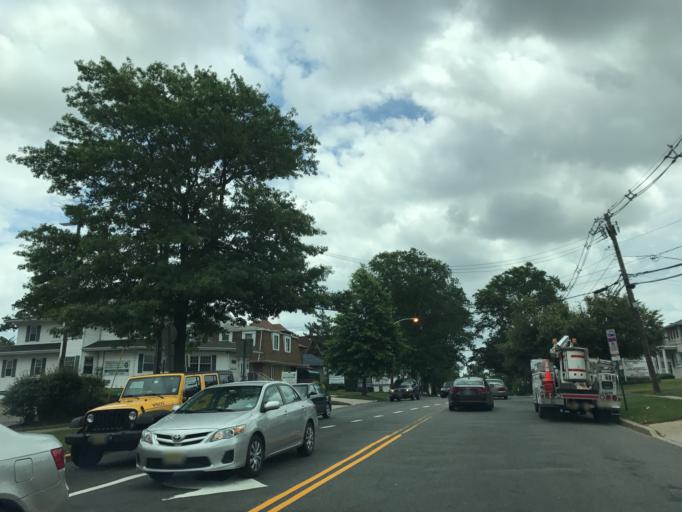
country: US
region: New Jersey
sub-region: Union County
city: Winfield
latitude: 40.6371
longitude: -74.2643
